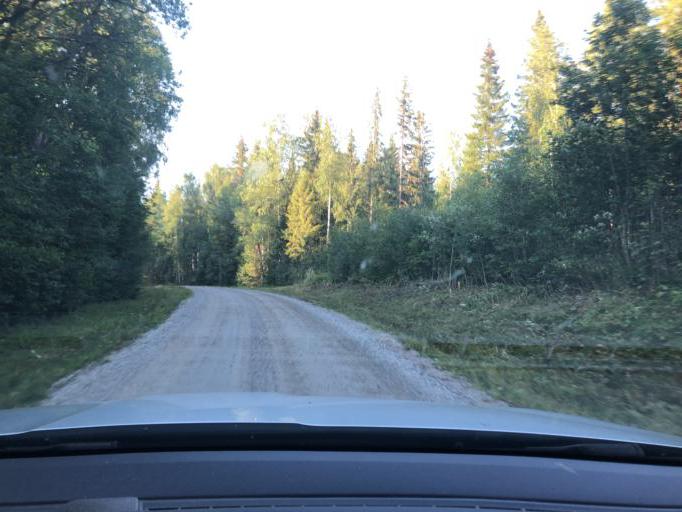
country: SE
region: Vaesternorrland
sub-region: Kramfors Kommun
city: Bollstabruk
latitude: 63.0483
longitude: 17.6917
